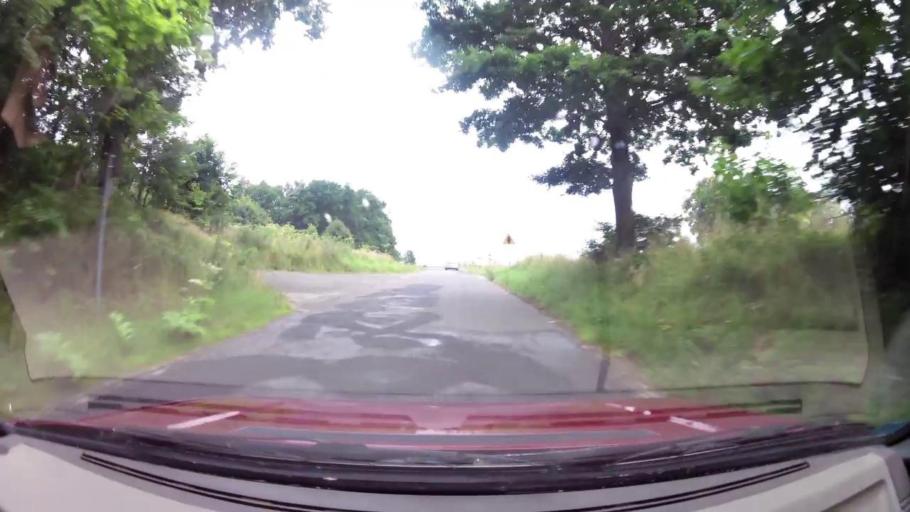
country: PL
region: West Pomeranian Voivodeship
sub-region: Powiat bialogardzki
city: Bialogard
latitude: 53.9419
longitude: 15.9577
